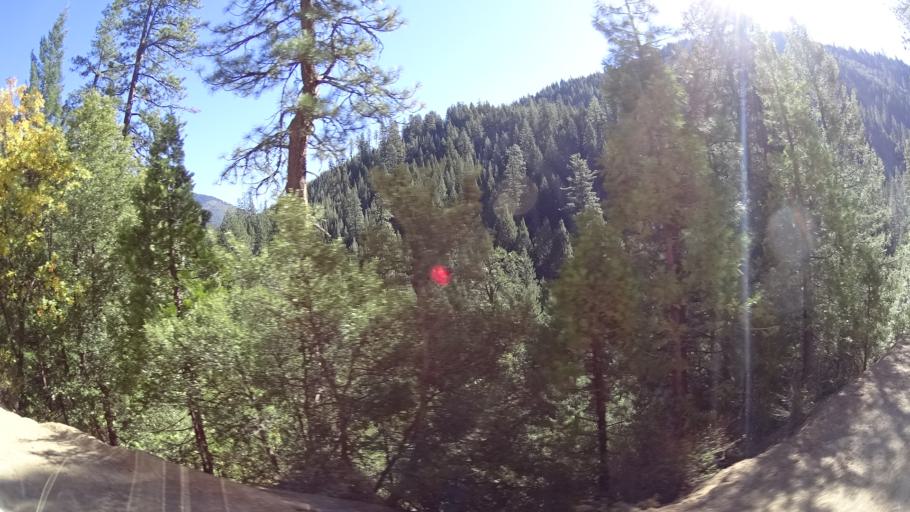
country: US
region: California
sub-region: Trinity County
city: Weaverville
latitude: 41.2220
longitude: -123.0095
